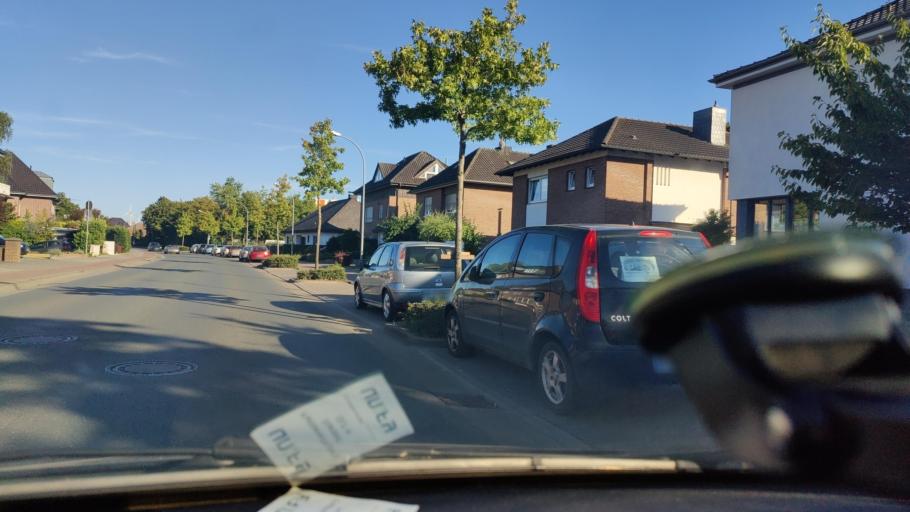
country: DE
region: North Rhine-Westphalia
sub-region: Regierungsbezirk Dusseldorf
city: Goch
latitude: 51.6736
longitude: 6.1548
